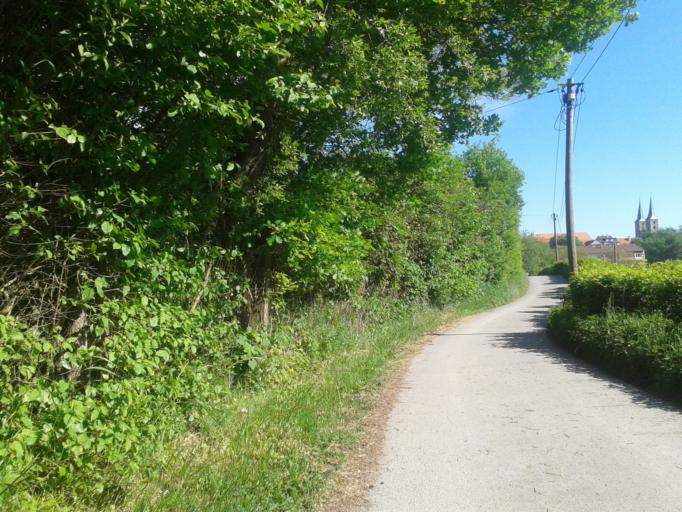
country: DE
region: Bavaria
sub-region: Upper Franconia
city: Bamberg
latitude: 49.8880
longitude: 10.8744
